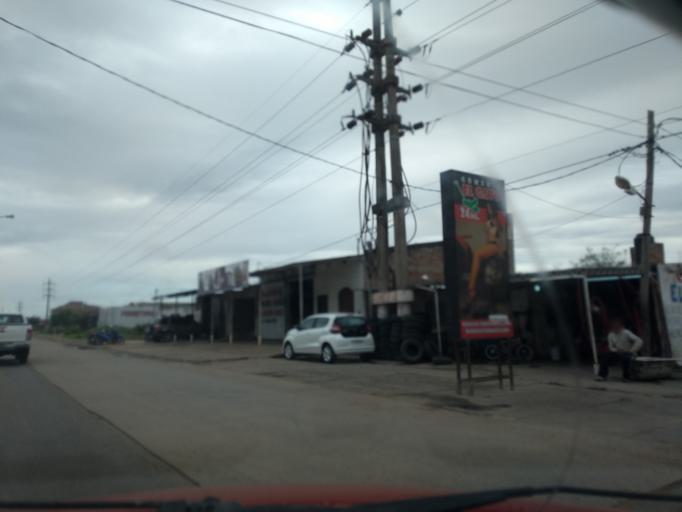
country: AR
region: Chaco
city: Barranqueras
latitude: -27.4831
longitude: -58.9648
